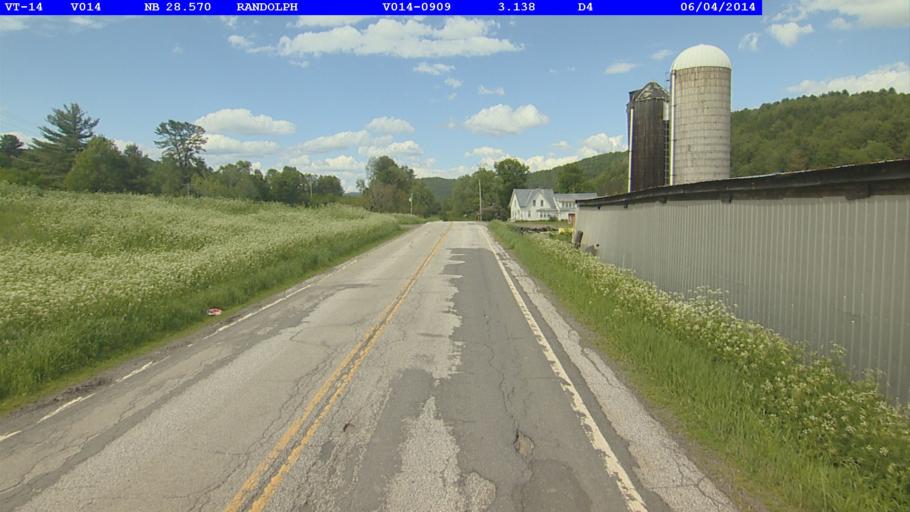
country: US
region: Vermont
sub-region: Orange County
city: Randolph
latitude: 43.9150
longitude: -72.5569
